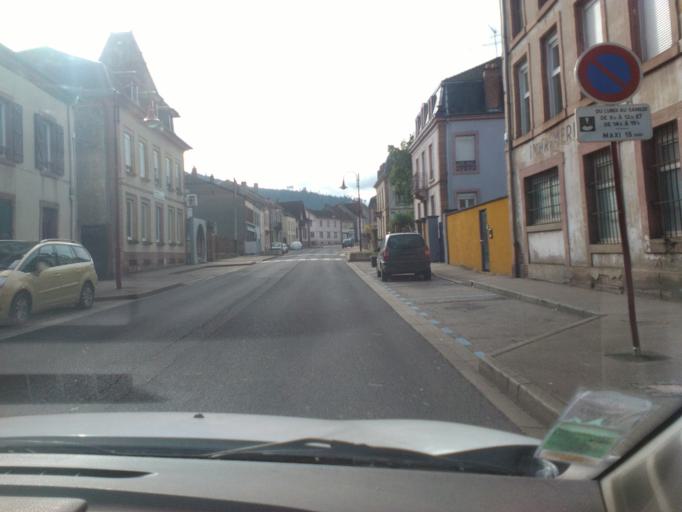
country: FR
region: Lorraine
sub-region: Departement des Vosges
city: Etival-Clairefontaine
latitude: 48.4054
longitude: 6.8409
